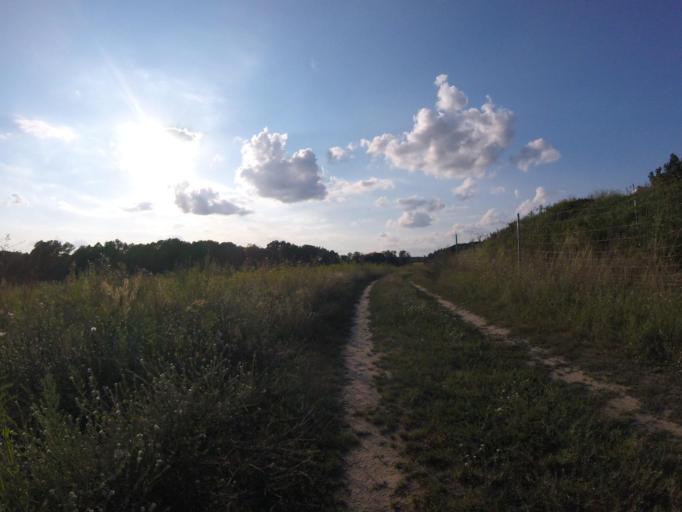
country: DE
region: Brandenburg
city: Mittenwalde
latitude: 52.2755
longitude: 13.5136
